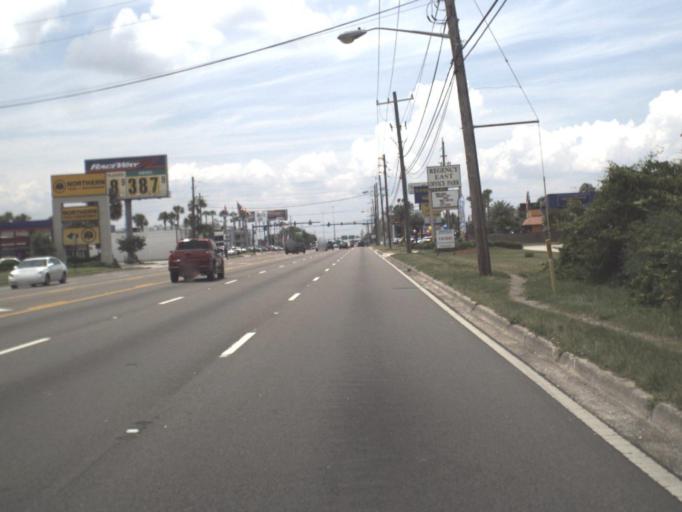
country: US
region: Florida
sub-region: Duval County
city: Jacksonville
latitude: 30.3228
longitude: -81.5399
